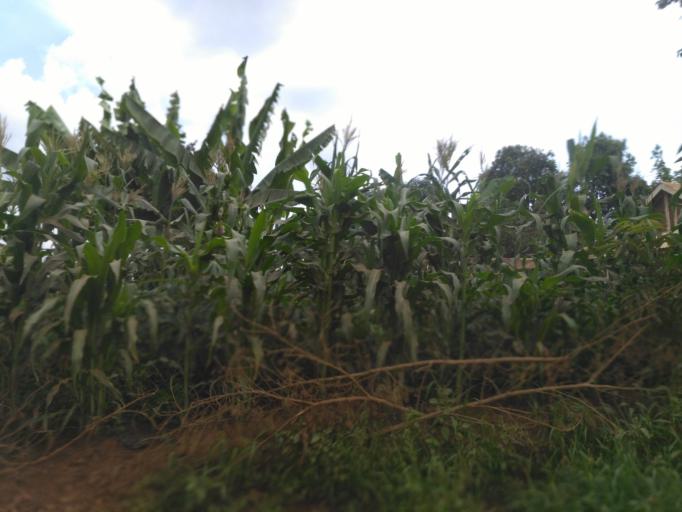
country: UG
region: Central Region
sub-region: Wakiso District
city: Bweyogerere
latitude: 0.4663
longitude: 32.6242
